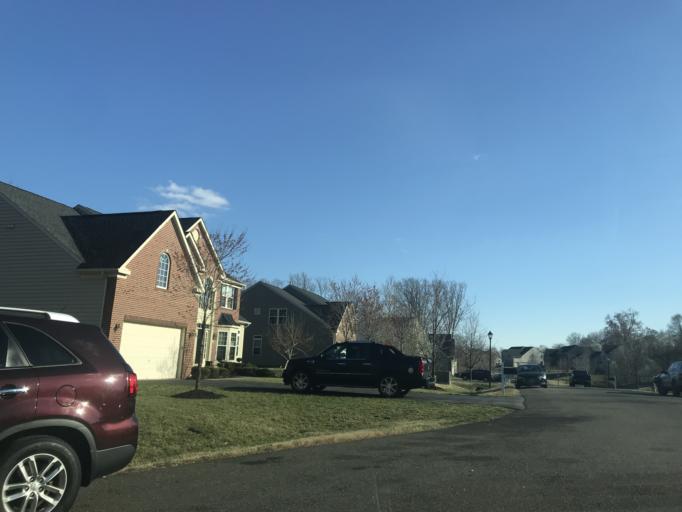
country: US
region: Maryland
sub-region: Prince George's County
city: Woodmore
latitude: 38.9133
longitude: -76.7930
